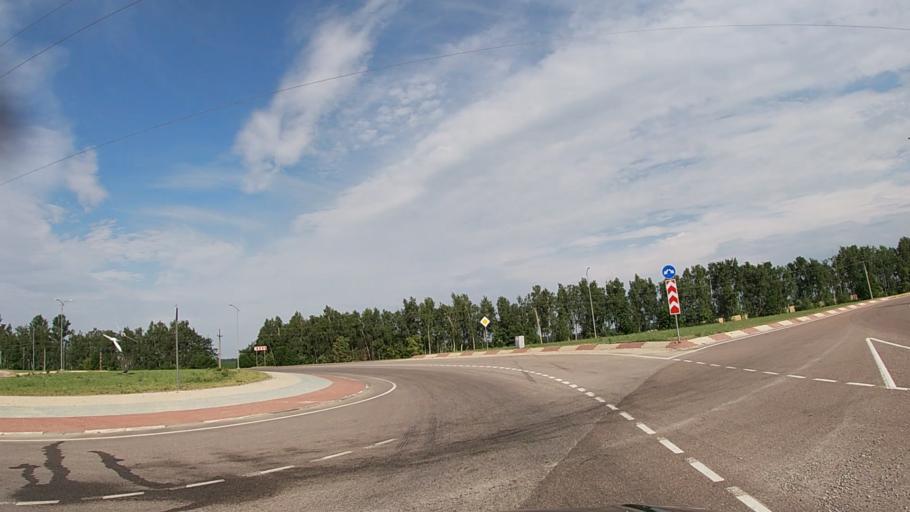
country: RU
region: Belgorod
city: Proletarskiy
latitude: 50.8308
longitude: 35.7676
